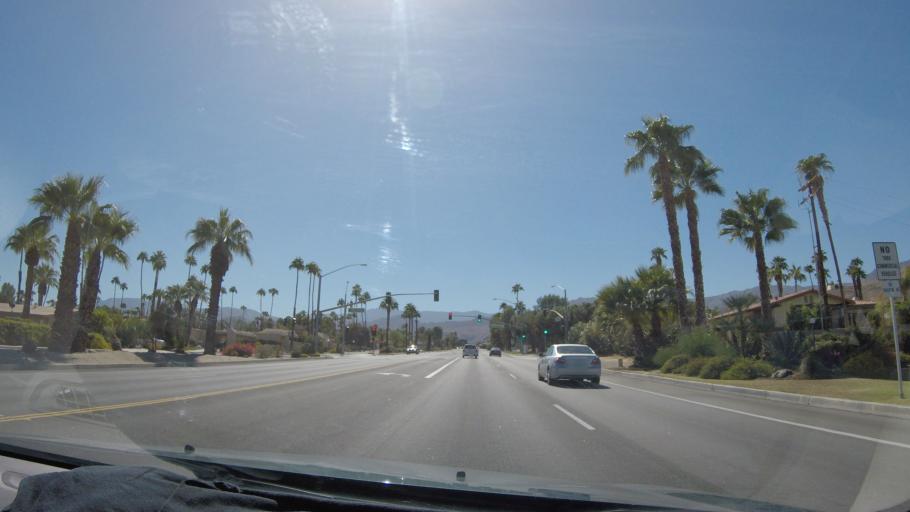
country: US
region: California
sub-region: Riverside County
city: Palm Desert
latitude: 33.7121
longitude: -116.3938
